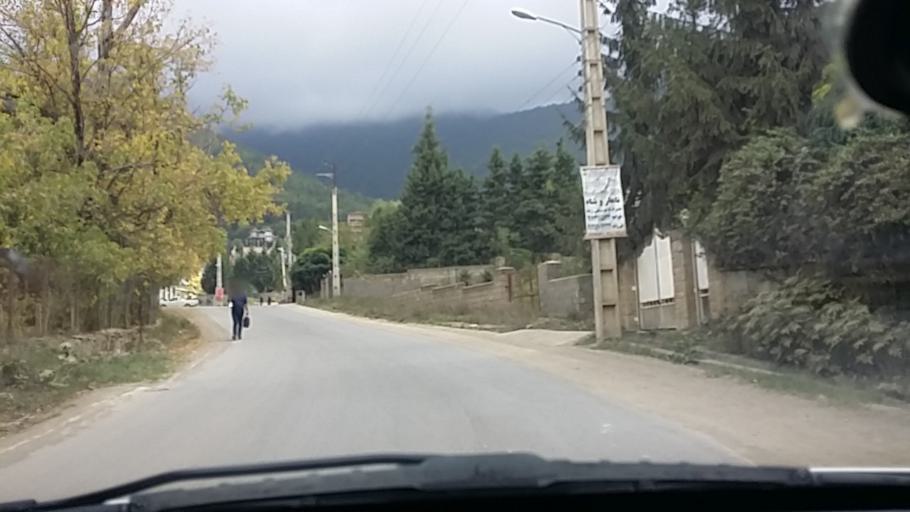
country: IR
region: Mazandaran
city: `Abbasabad
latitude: 36.4977
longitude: 51.1640
